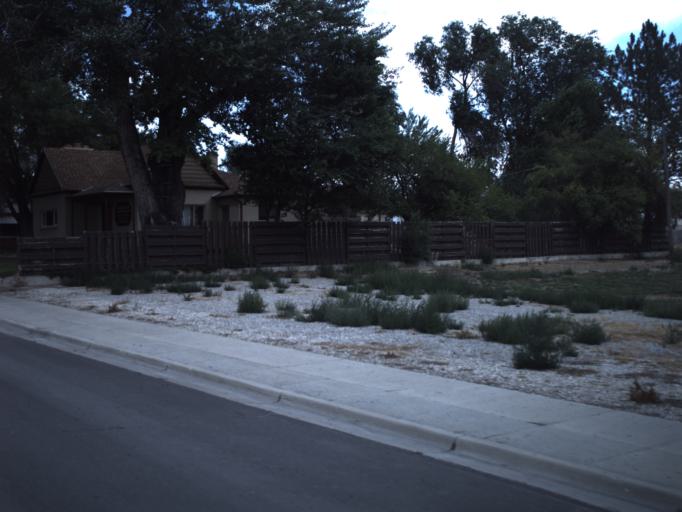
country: US
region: Utah
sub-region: Sanpete County
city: Gunnison
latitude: 39.1509
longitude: -111.8183
